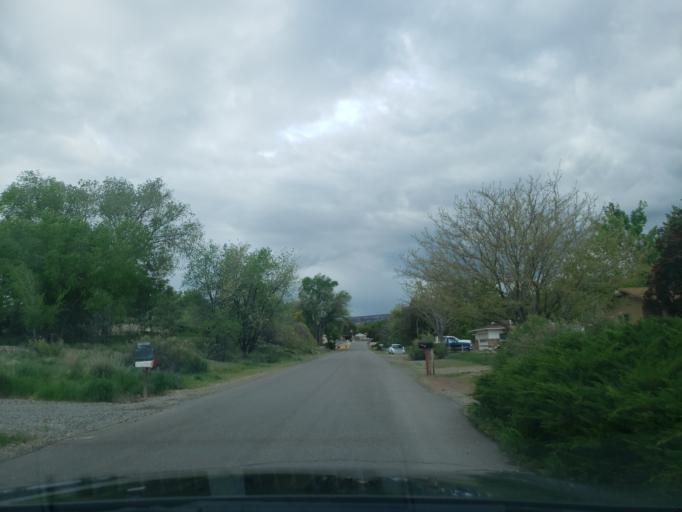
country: US
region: Colorado
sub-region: Mesa County
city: Redlands
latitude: 39.1021
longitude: -108.6616
